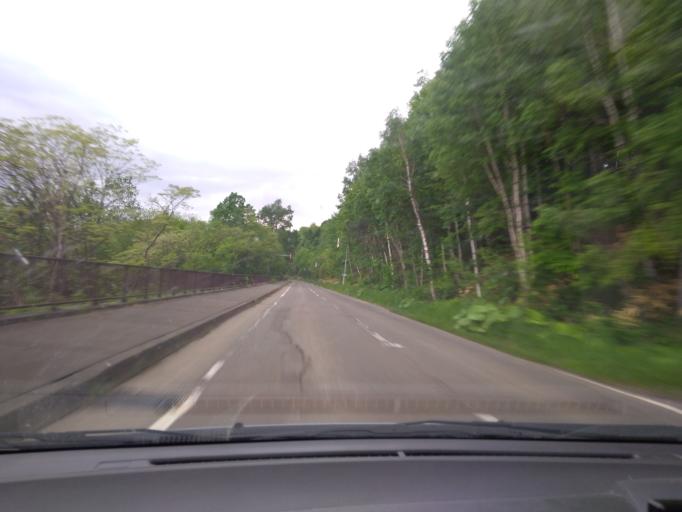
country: JP
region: Hokkaido
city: Shimo-furano
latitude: 43.1748
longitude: 142.5573
